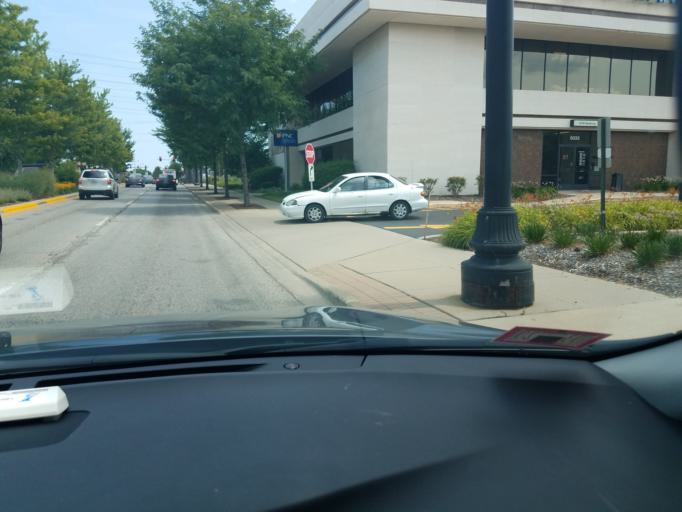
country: US
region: Illinois
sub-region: Cook County
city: Skokie
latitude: 42.0407
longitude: -87.7539
